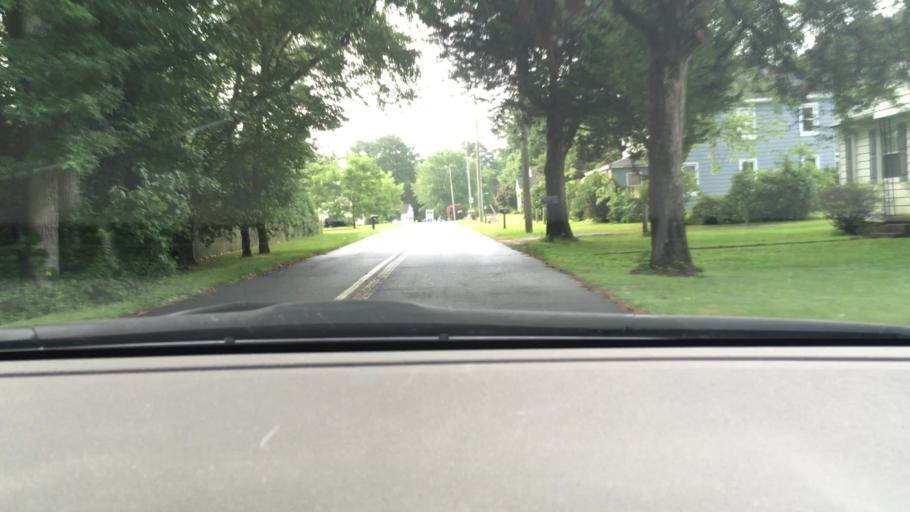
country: US
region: Maryland
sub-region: Wicomico County
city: Fruitland
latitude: 38.3375
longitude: -75.6307
